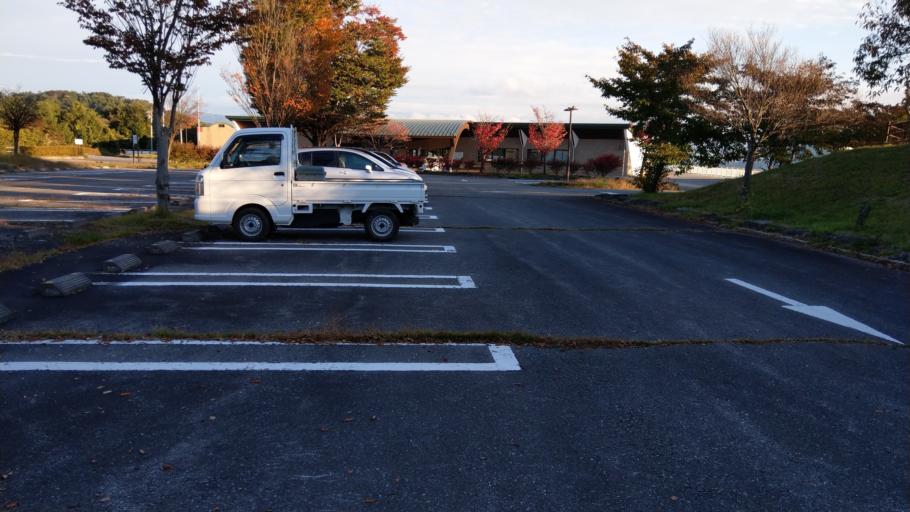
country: JP
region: Nagano
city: Komoro
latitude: 36.3422
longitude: 138.4223
